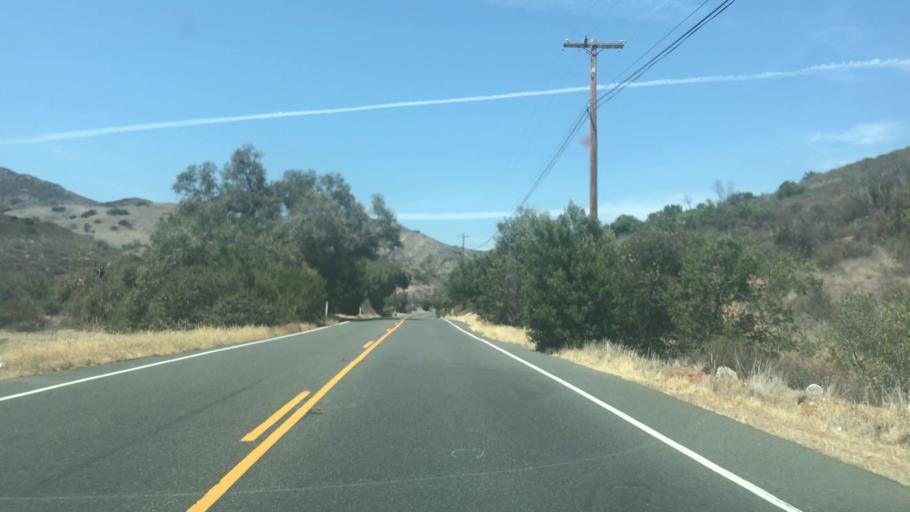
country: US
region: California
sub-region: Orange County
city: Coto De Caza
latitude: 33.5716
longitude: -117.5423
